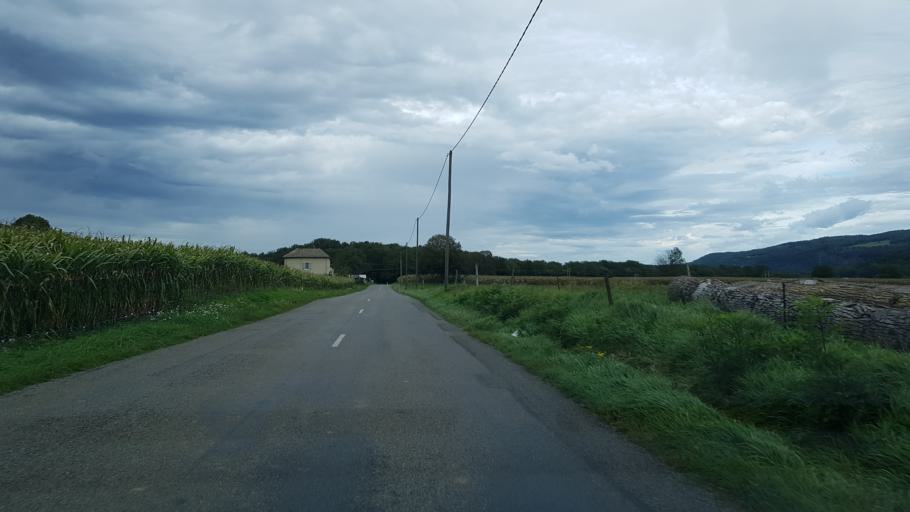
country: FR
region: Rhone-Alpes
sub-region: Departement de l'Ain
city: Villereversure
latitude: 46.2026
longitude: 5.3993
